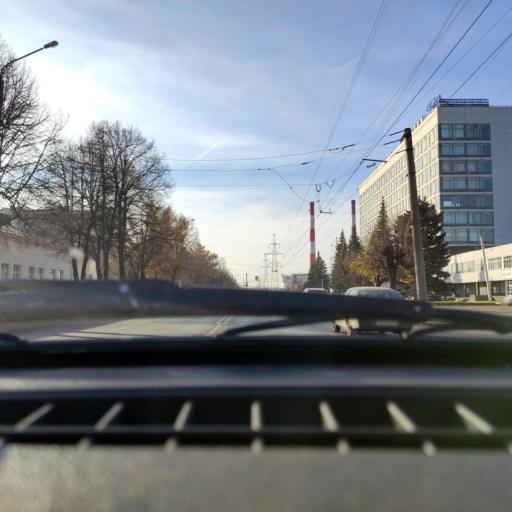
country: RU
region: Bashkortostan
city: Ufa
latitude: 54.7881
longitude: 56.1337
